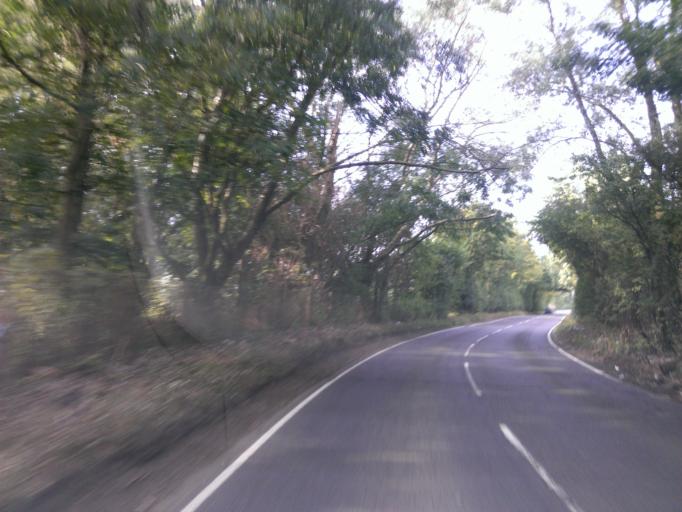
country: GB
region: England
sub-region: Essex
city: Witham
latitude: 51.8126
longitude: 0.6702
